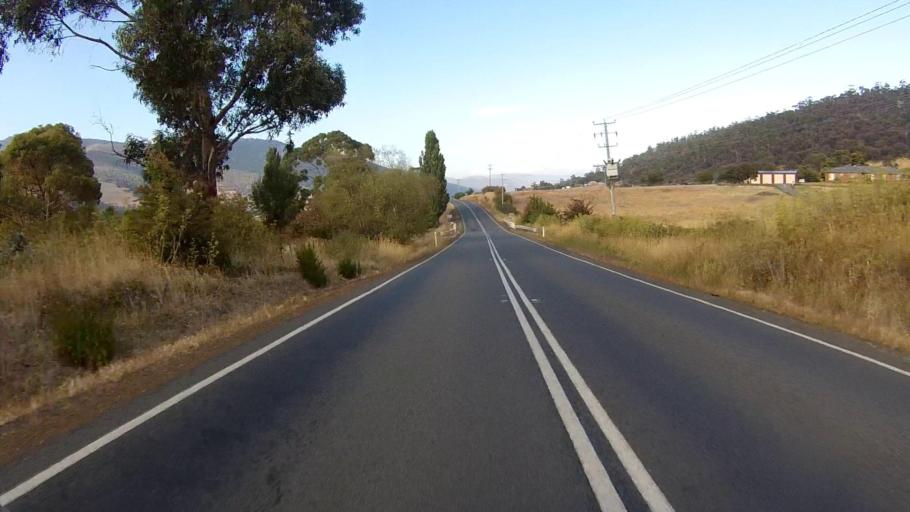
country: AU
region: Tasmania
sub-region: Brighton
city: Bridgewater
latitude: -42.7346
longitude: 147.1753
